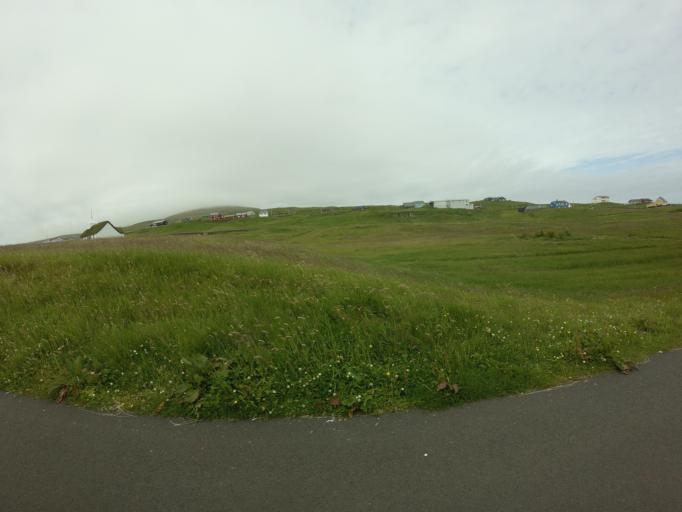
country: FO
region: Sandoy
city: Sandur
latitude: 61.8300
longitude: -6.6673
